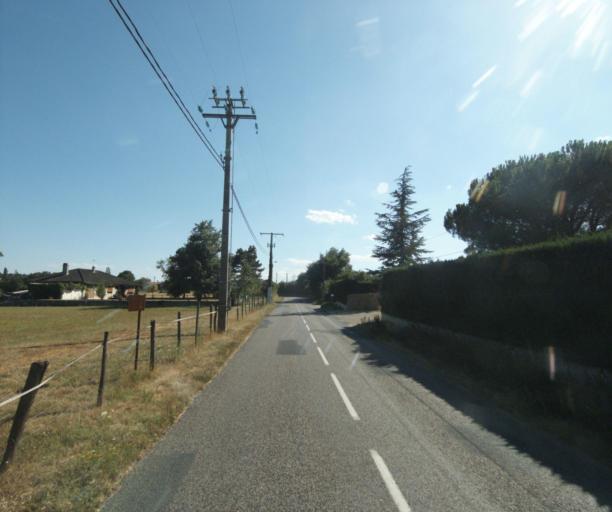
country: FR
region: Rhone-Alpes
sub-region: Departement du Rhone
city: La Tour-de-Salvagny
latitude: 45.8385
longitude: 4.7211
